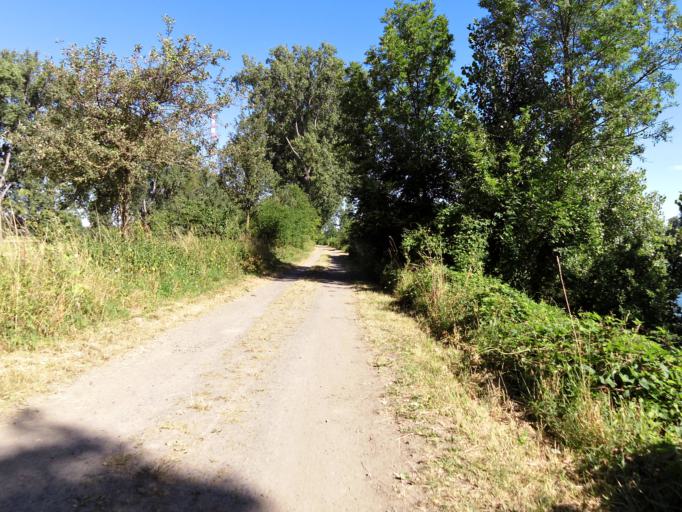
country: DE
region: Rheinland-Pfalz
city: Bobenheim-Roxheim
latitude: 49.6041
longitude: 8.4075
